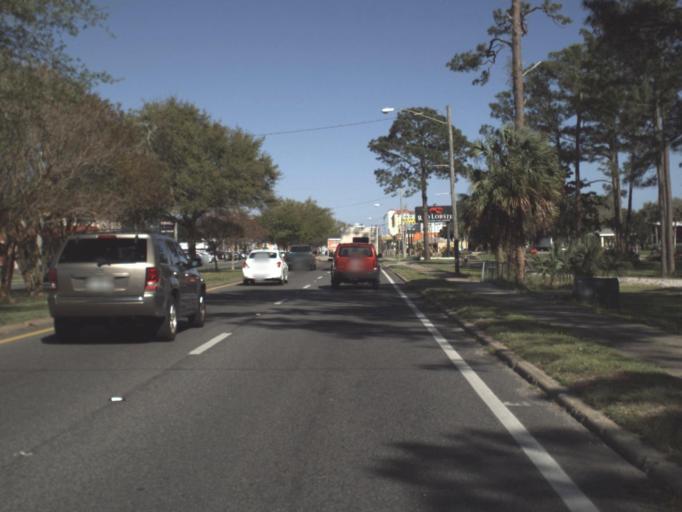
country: US
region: Florida
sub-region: Okaloosa County
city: Fort Walton Beach
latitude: 30.4070
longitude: -86.6365
